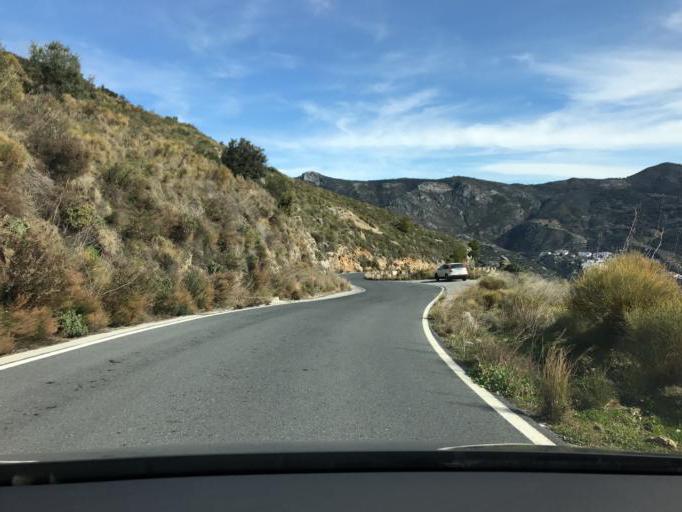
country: ES
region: Andalusia
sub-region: Provincia de Granada
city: Otivar
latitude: 36.8320
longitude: -3.7008
